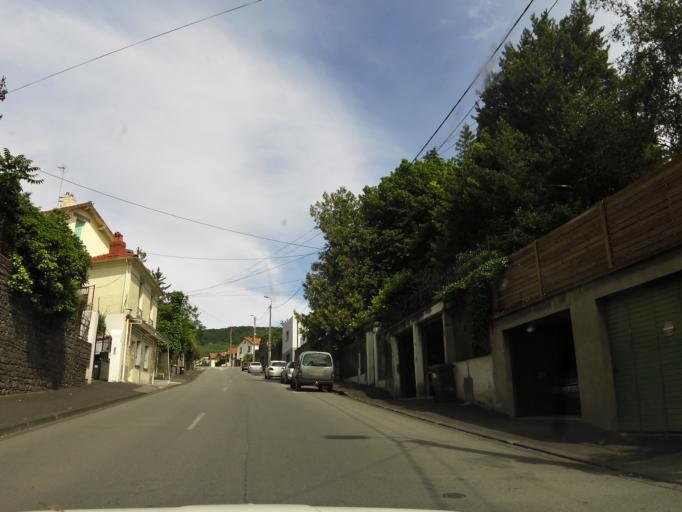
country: FR
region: Auvergne
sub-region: Departement du Puy-de-Dome
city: Clermont-Ferrand
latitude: 45.7905
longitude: 3.0783
